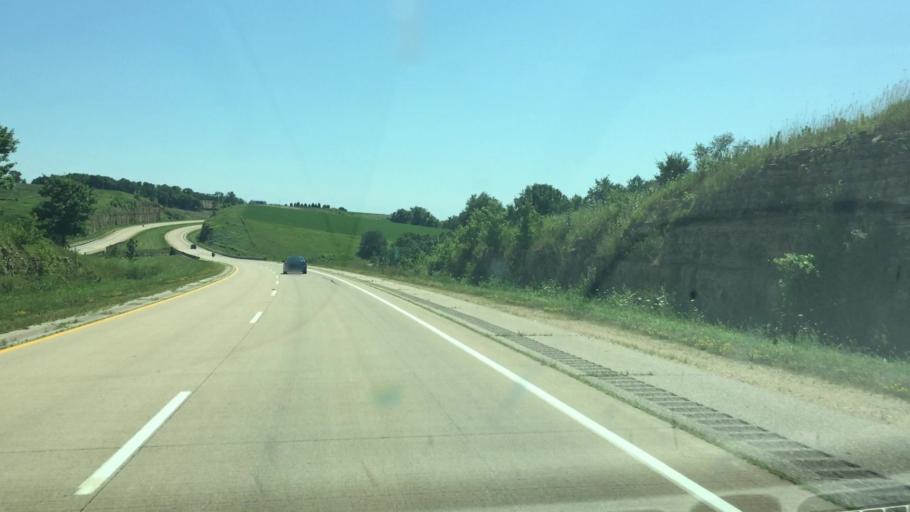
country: US
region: Wisconsin
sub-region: Iowa County
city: Mineral Point
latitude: 42.8750
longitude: -90.1919
